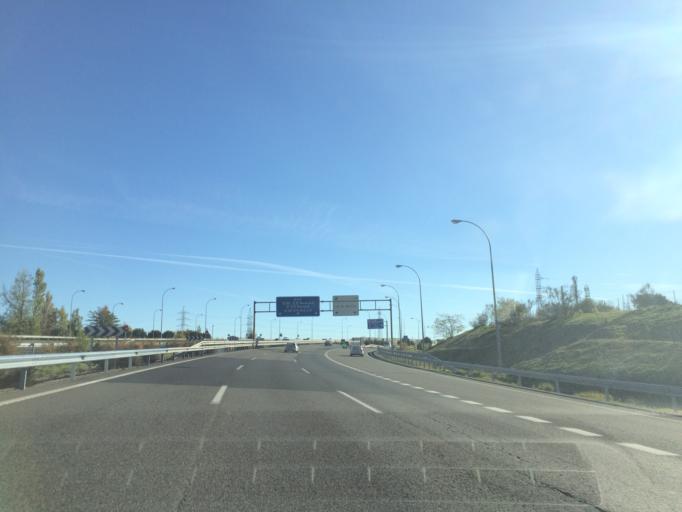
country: ES
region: Madrid
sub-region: Provincia de Madrid
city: Pozuelo de Alarcon
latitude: 40.4144
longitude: -3.8220
